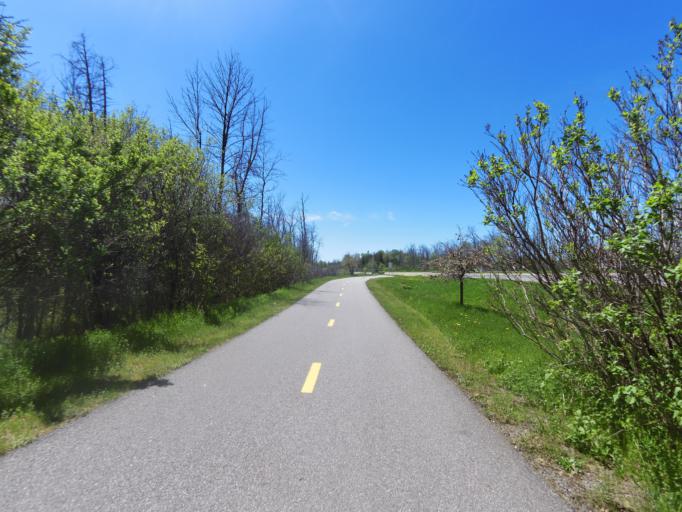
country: CA
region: Ontario
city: Bells Corners
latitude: 45.4138
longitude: -75.8267
